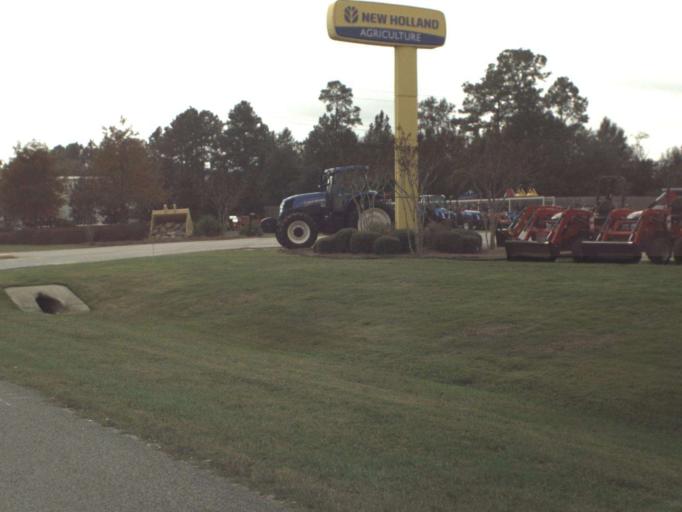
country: US
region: Florida
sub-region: Escambia County
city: Gonzalez
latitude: 30.5513
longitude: -87.2833
